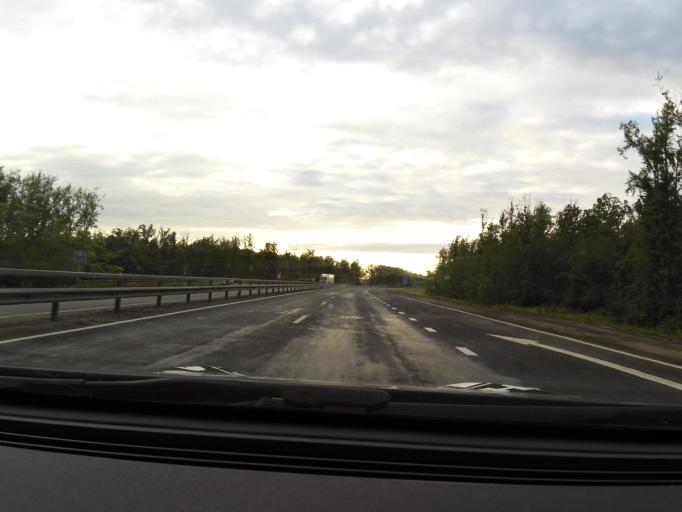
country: RU
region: Chuvashia
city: Kugesi
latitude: 55.9450
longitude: 47.3787
